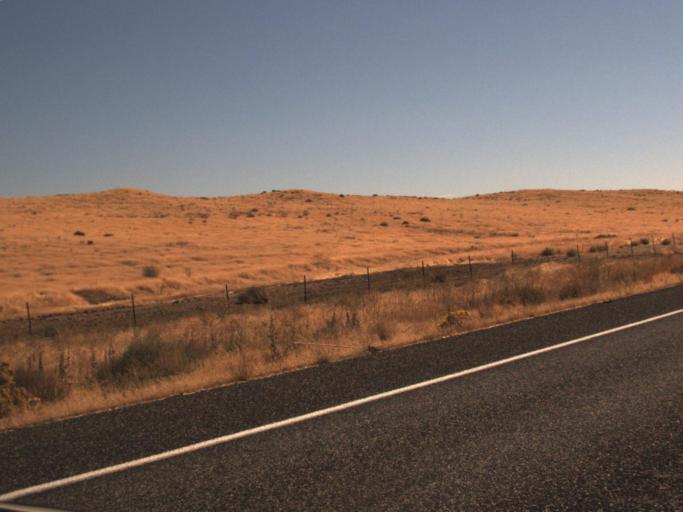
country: US
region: Washington
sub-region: Benton County
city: Benton City
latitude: 46.4494
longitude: -119.5039
